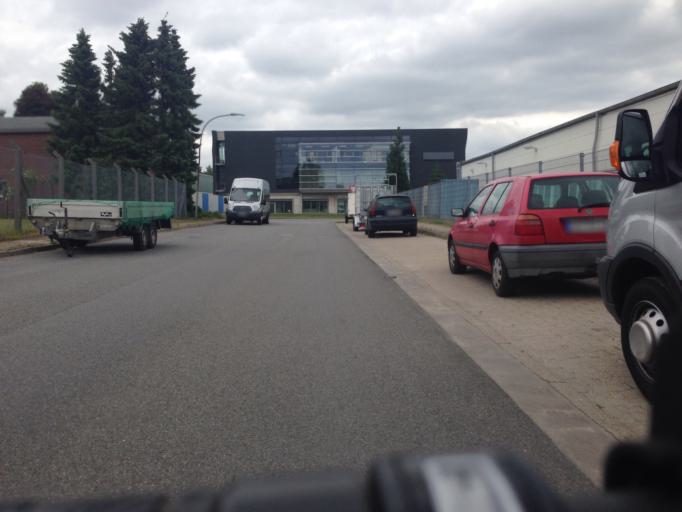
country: DE
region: Schleswig-Holstein
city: Barsbuettel
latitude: 53.5718
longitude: 10.1868
